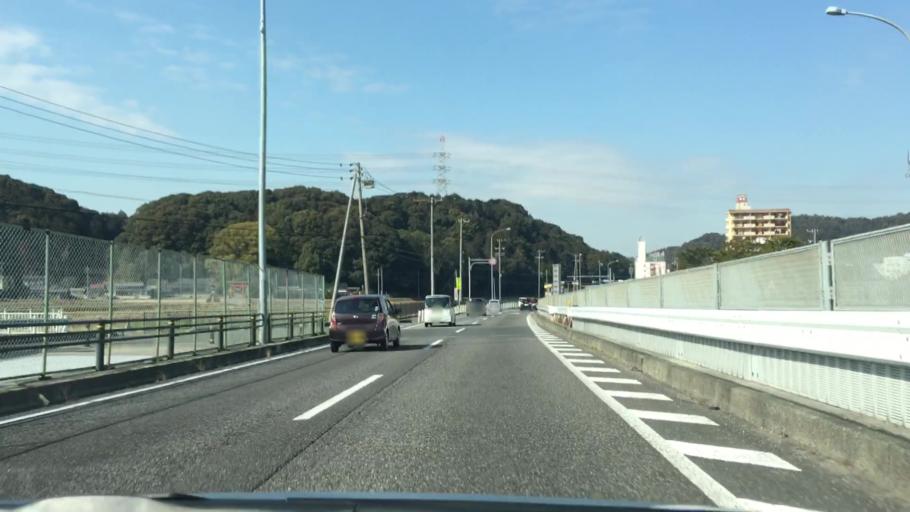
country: JP
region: Aichi
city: Gamagori
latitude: 34.9016
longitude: 137.2373
